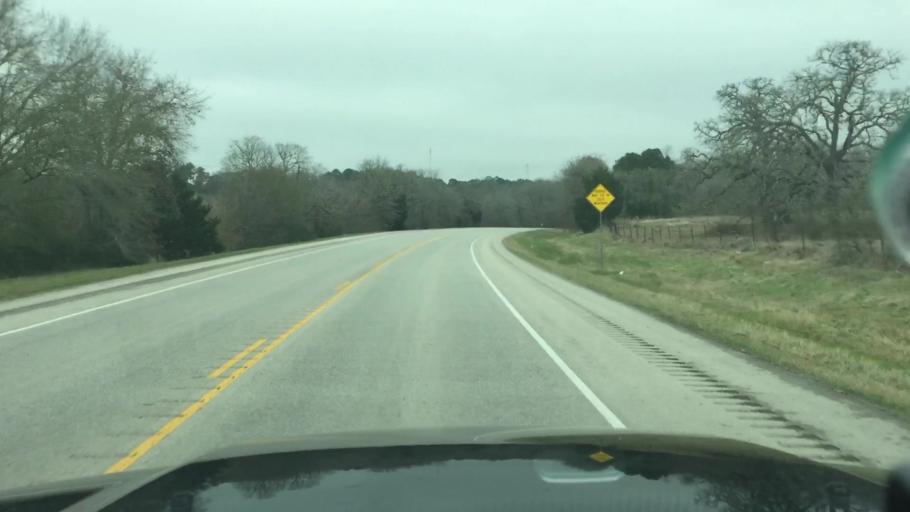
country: US
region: Texas
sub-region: Fayette County
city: La Grange
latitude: 30.0322
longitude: -96.9081
